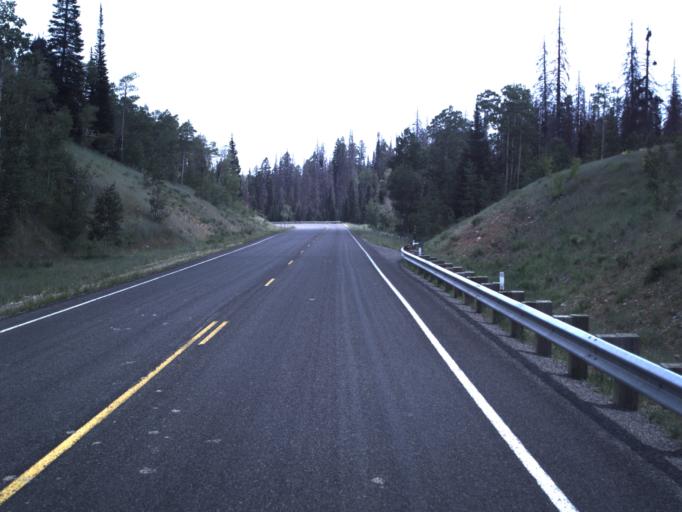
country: US
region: Utah
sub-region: Summit County
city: Francis
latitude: 40.4843
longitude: -110.9516
